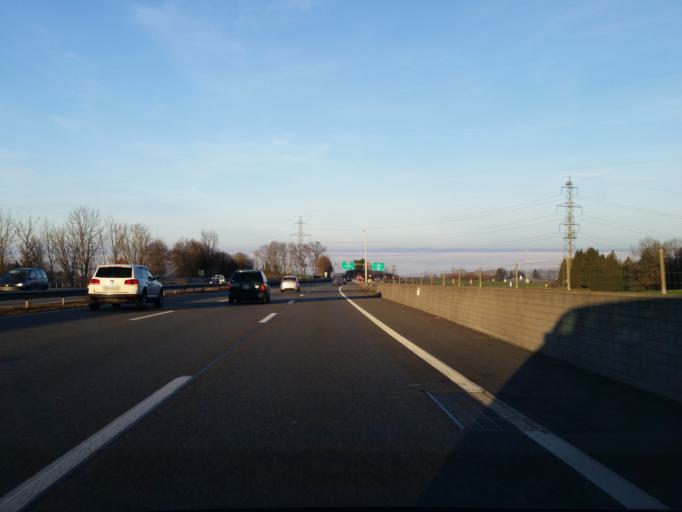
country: CH
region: Saint Gallen
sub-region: Wahlkreis Rorschach
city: Morschwil
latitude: 47.4645
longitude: 9.4390
